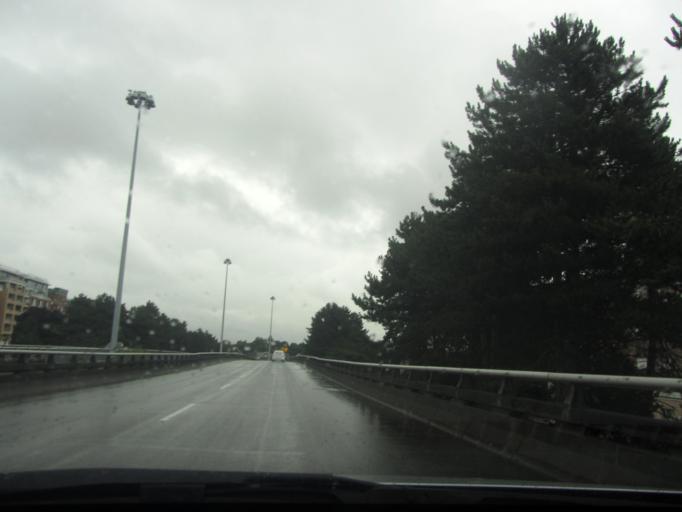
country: CA
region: British Columbia
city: Vancouver
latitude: 49.2771
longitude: -123.1008
